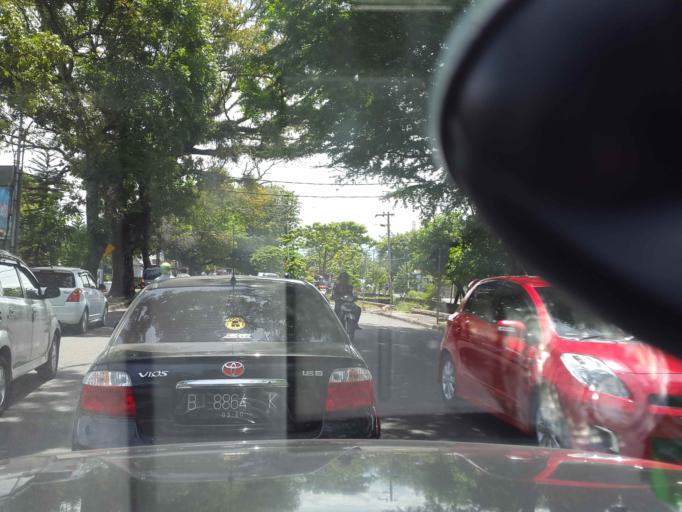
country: ID
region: West Sumatra
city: Padang
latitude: -0.9398
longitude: 100.3661
